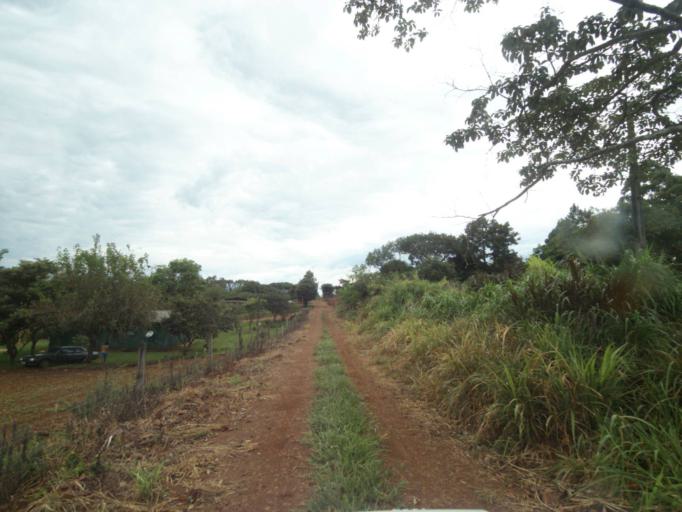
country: BR
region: Parana
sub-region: Guaraniacu
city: Guaraniacu
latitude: -24.9083
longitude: -52.9363
